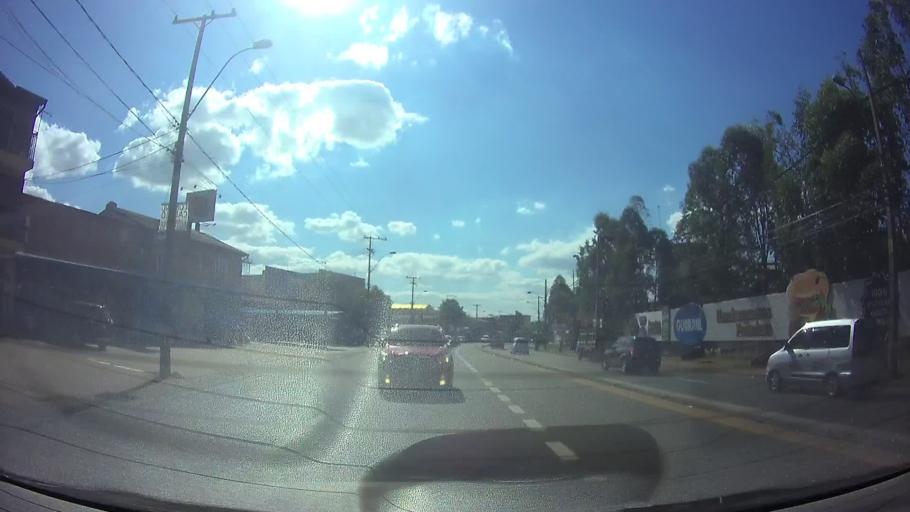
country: PY
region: Central
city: Itaugua
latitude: -25.3962
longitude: -57.3464
